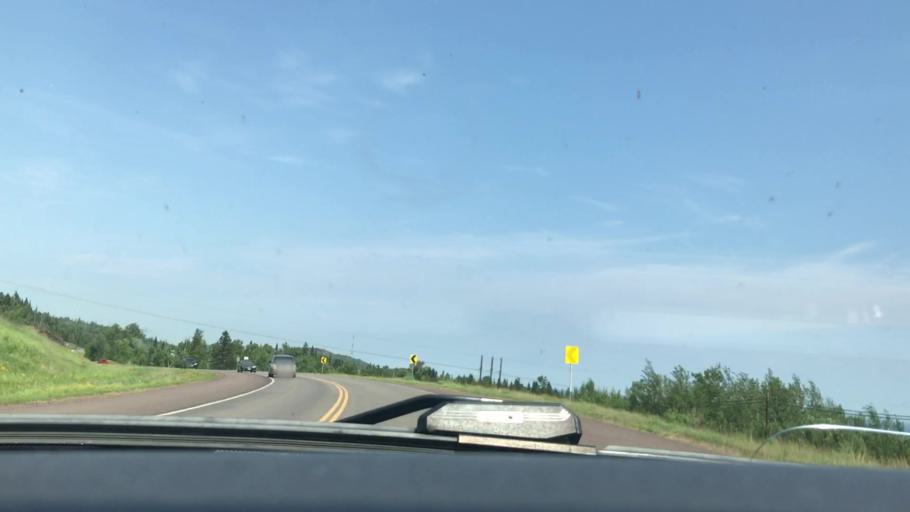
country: US
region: Minnesota
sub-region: Lake County
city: Silver Bay
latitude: 47.3045
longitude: -91.2443
